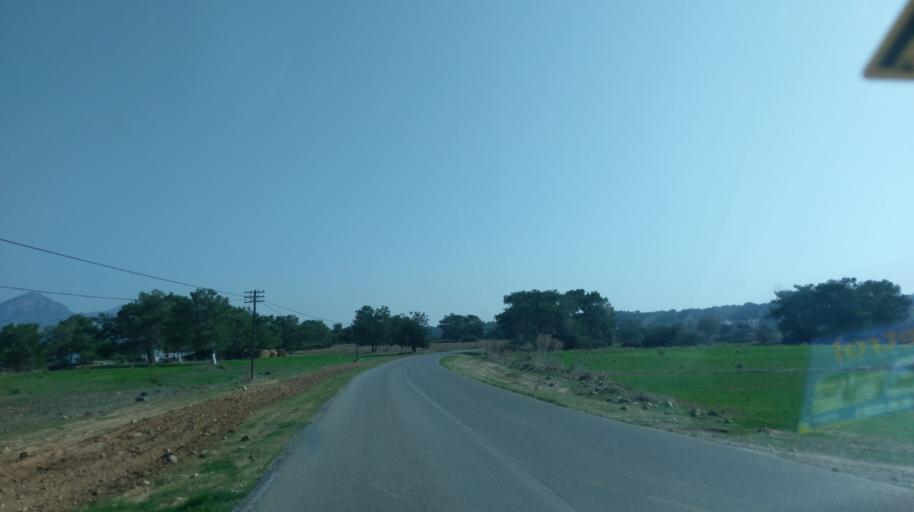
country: CY
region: Keryneia
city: Lapithos
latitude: 35.3261
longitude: 33.0454
